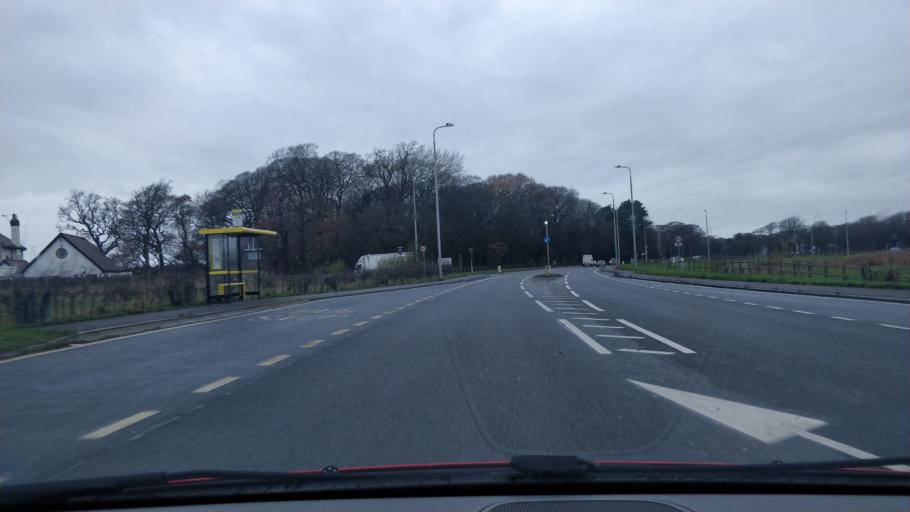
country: GB
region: England
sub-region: Sefton
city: Thornton
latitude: 53.5059
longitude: -3.0065
